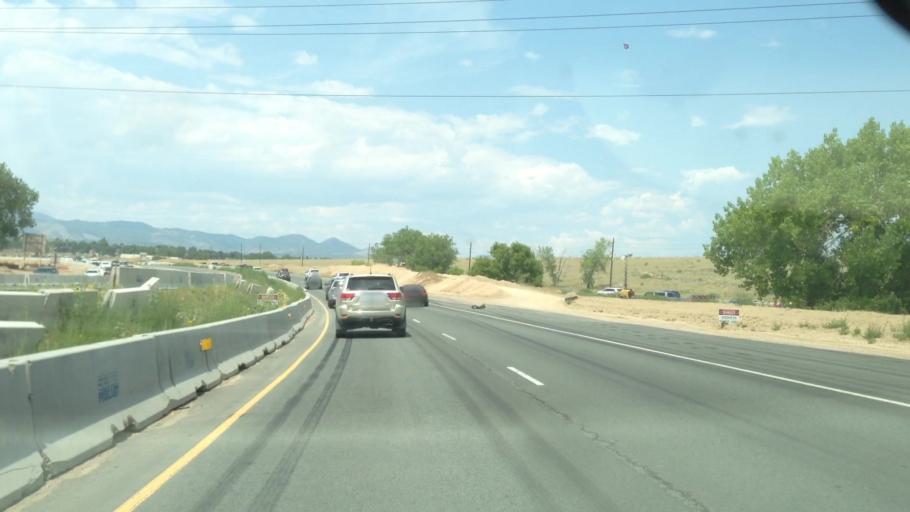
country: US
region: Colorado
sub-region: Jefferson County
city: Columbine
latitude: 39.5676
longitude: -105.0440
